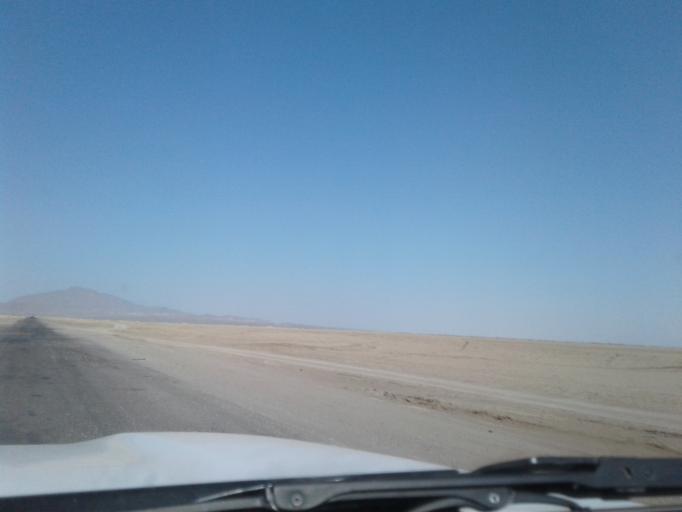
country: TM
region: Balkan
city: Gumdag
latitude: 39.2208
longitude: 54.6585
